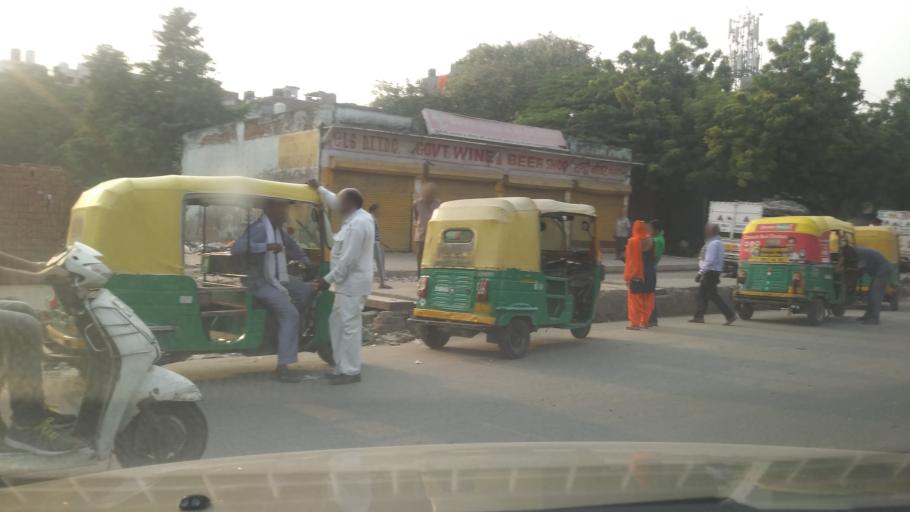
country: IN
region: Uttar Pradesh
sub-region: Gautam Buddha Nagar
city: Noida
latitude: 28.5333
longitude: 77.2688
